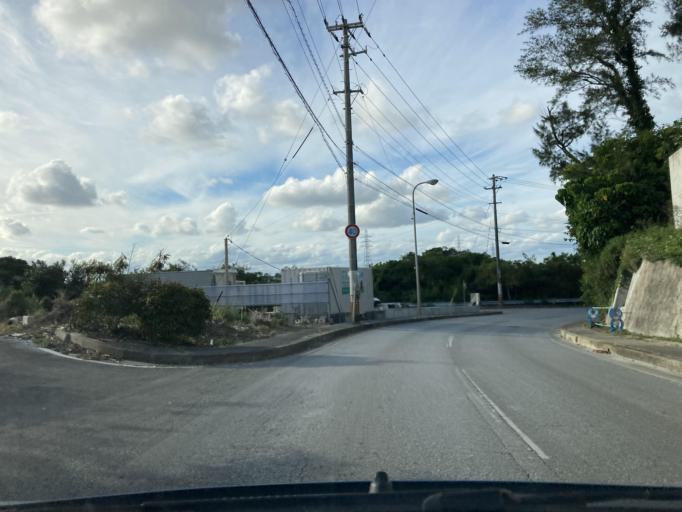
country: JP
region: Okinawa
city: Tomigusuku
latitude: 26.1466
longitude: 127.7445
